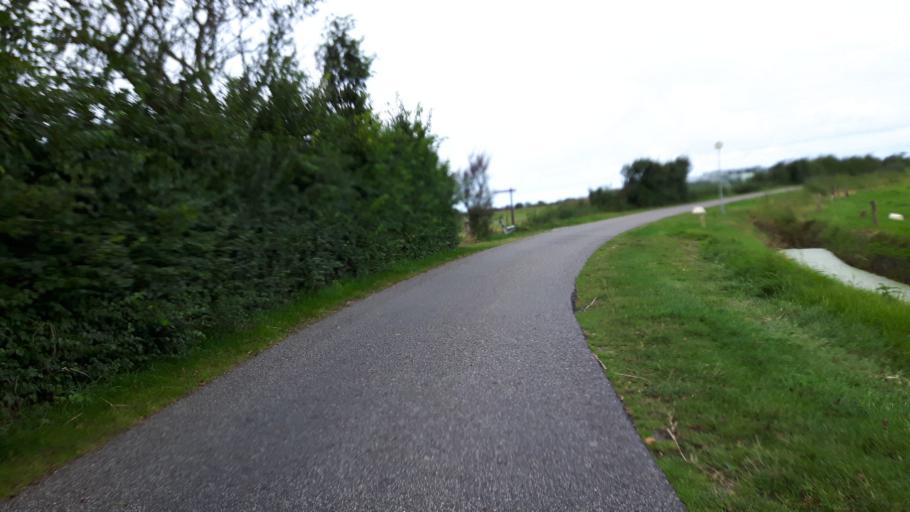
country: NL
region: Friesland
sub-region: Gemeente Ameland
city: Hollum
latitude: 53.4437
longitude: 5.6760
